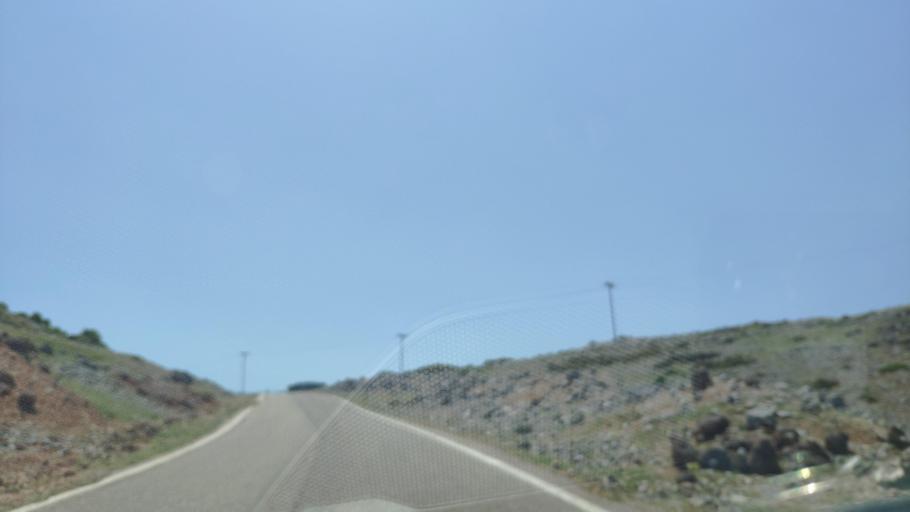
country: GR
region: West Greece
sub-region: Nomos Aitolias kai Akarnanias
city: Krikellos
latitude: 39.0512
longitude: 21.3720
